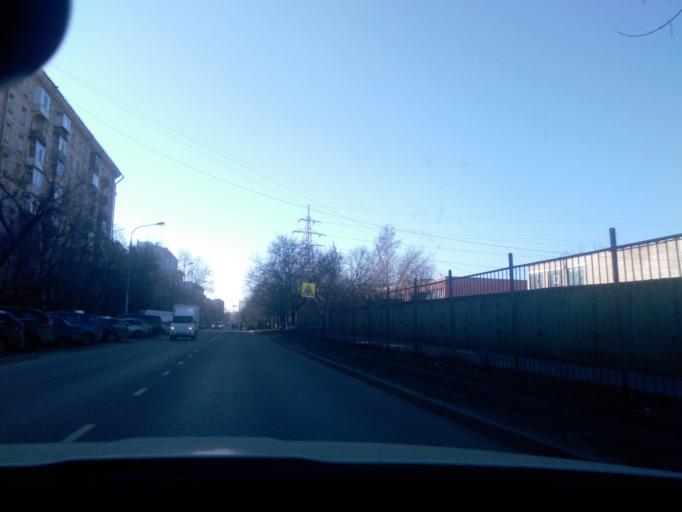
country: RU
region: Moscow
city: Sokol
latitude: 55.7851
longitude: 37.5100
